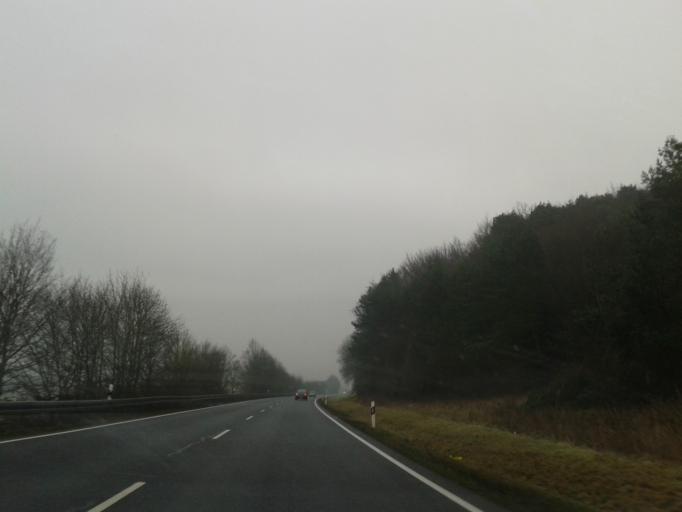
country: DE
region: Bavaria
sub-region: Regierungsbezirk Unterfranken
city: Burgpreppach
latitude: 50.1444
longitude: 10.6449
